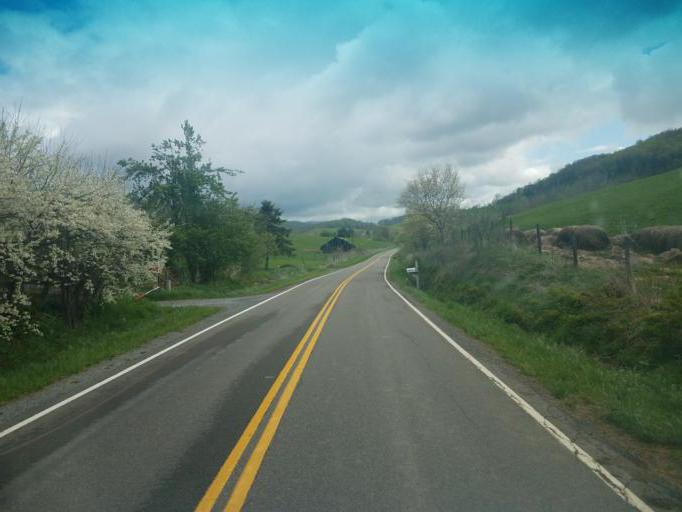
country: US
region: Virginia
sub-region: Smyth County
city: Atkins
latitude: 36.9944
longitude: -81.3817
